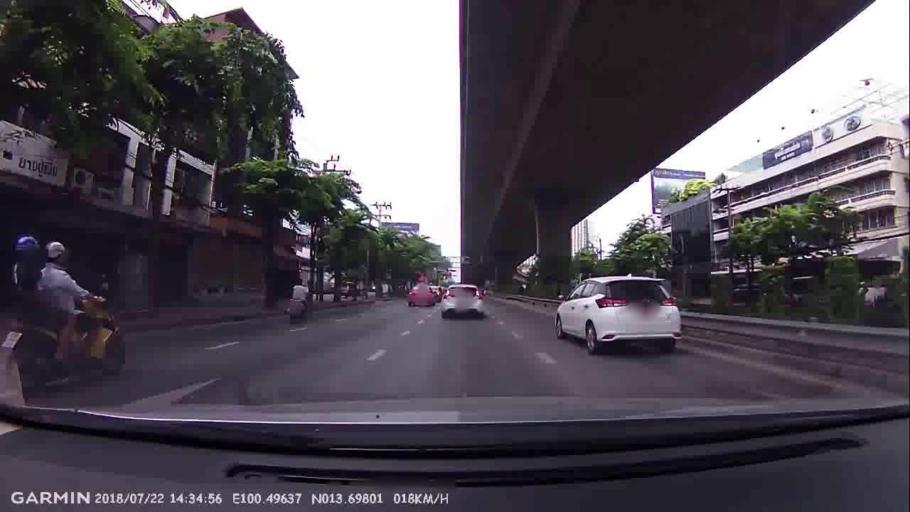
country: TH
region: Bangkok
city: Bang Kho Laem
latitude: 13.6980
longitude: 100.4964
